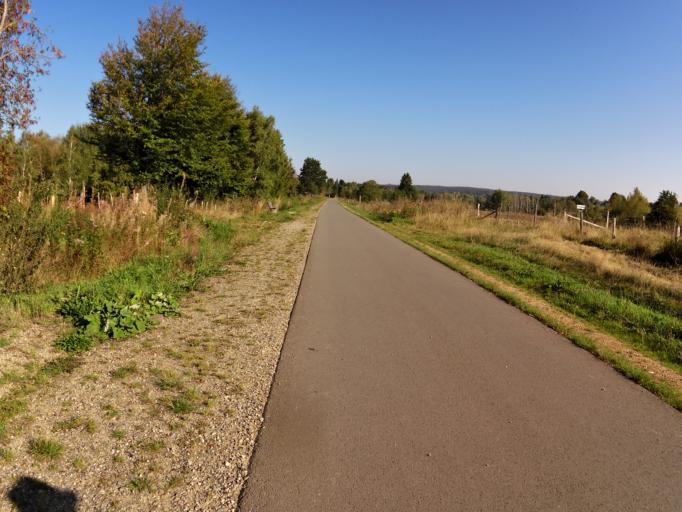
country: BE
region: Wallonia
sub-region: Province de Liege
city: Ambleve
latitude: 50.3409
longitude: 6.1206
